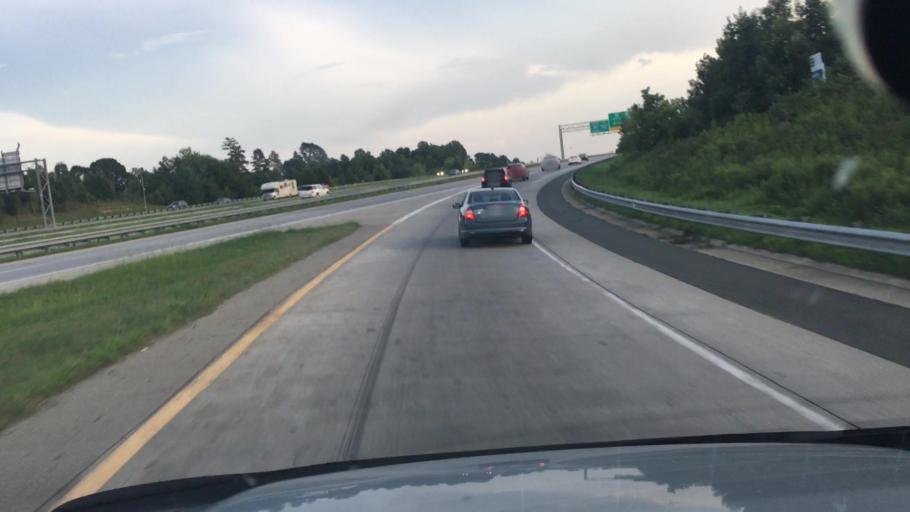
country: US
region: North Carolina
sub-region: Gaston County
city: Belmont
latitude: 35.2459
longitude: -80.9697
